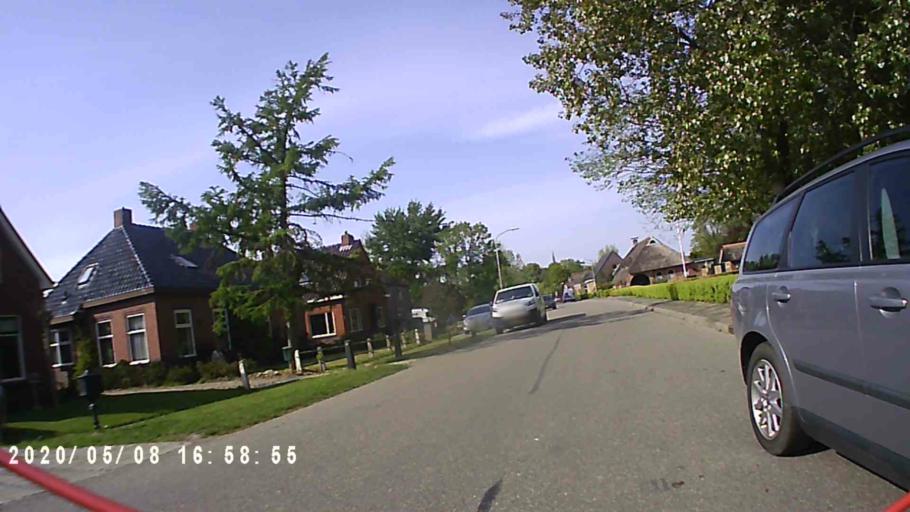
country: NL
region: Groningen
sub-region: Gemeente Bedum
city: Bedum
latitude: 53.3987
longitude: 6.6109
